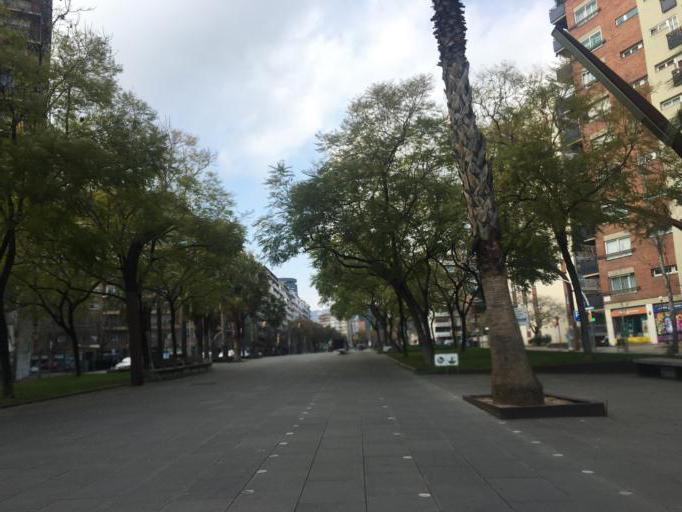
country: ES
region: Catalonia
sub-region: Provincia de Barcelona
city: les Corts
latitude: 41.3815
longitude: 2.1284
